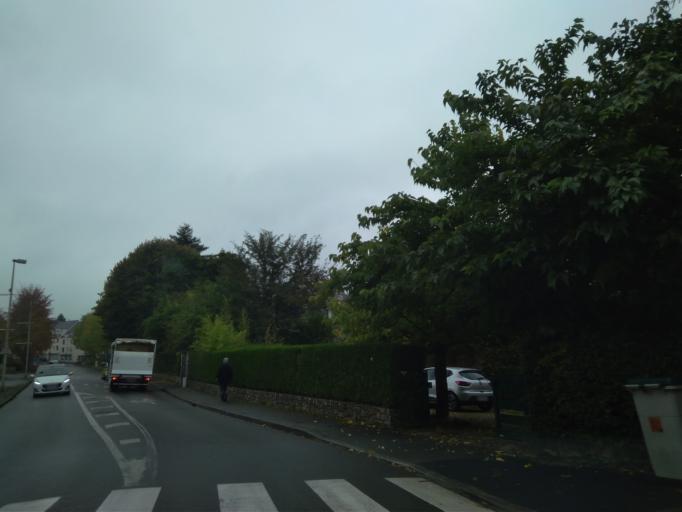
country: FR
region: Brittany
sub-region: Departement d'Ille-et-Vilaine
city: Saint-Gregoire
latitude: 48.1512
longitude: -1.6823
